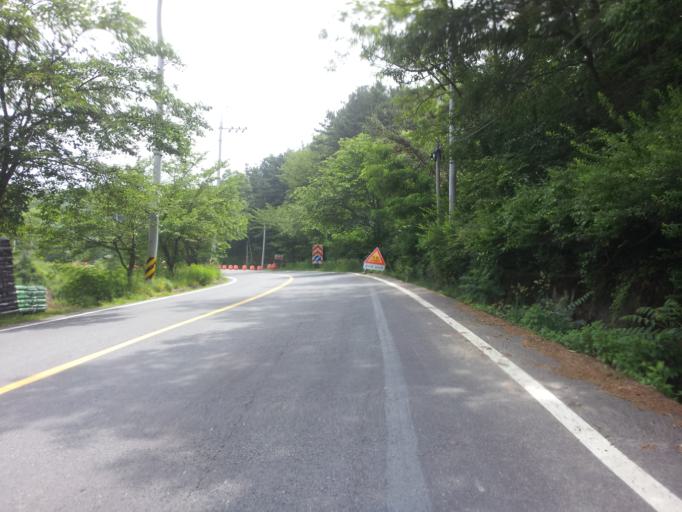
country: KR
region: Chungcheongbuk-do
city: Okcheon
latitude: 36.3816
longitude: 127.5171
